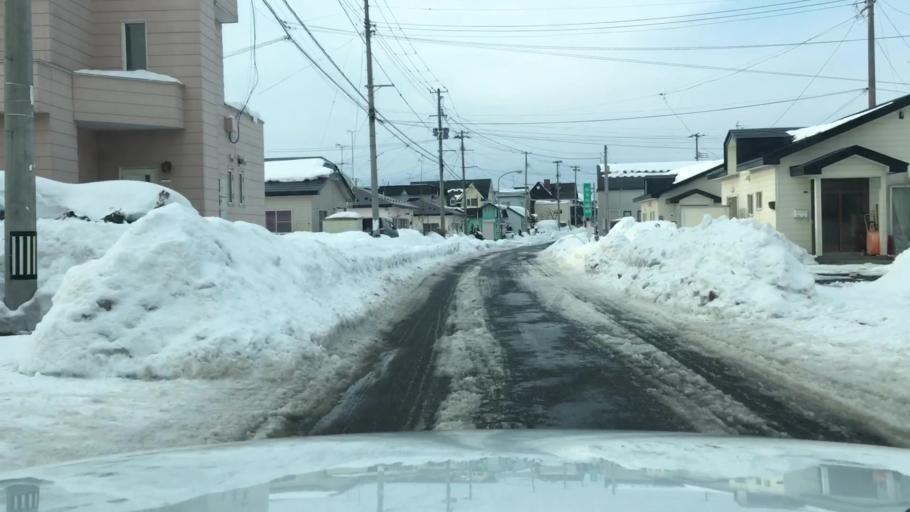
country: JP
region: Aomori
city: Hirosaki
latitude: 40.5770
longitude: 140.4898
